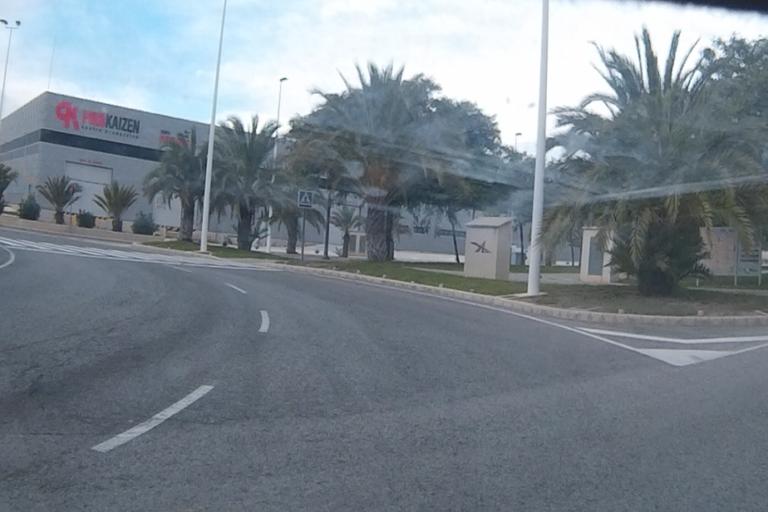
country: ES
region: Valencia
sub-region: Provincia de Alicante
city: Elche
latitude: 38.2971
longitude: -0.6164
